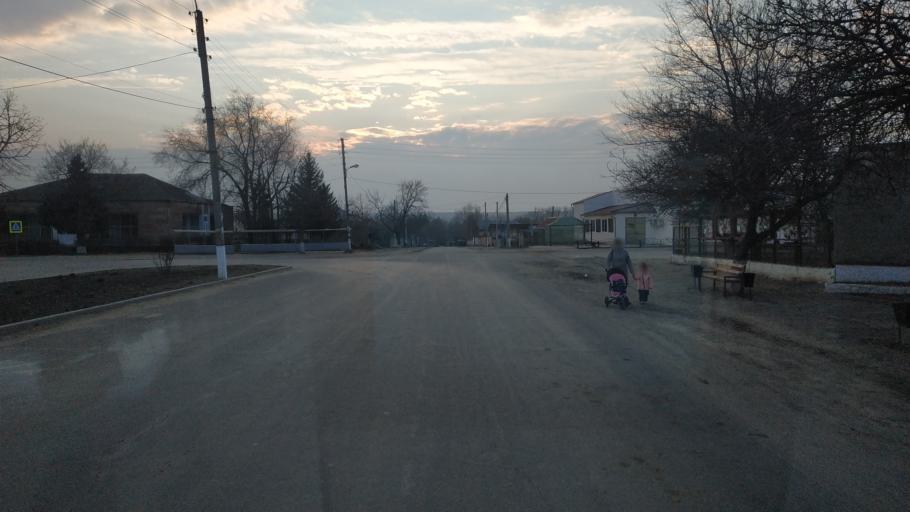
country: MD
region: Hincesti
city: Dancu
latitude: 46.6726
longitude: 28.3270
